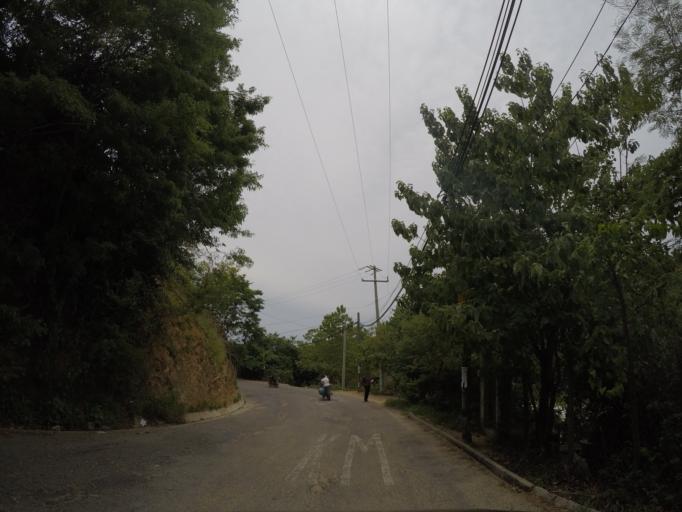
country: MX
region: Oaxaca
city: San Pedro Pochutla
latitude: 15.6672
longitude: -96.4962
